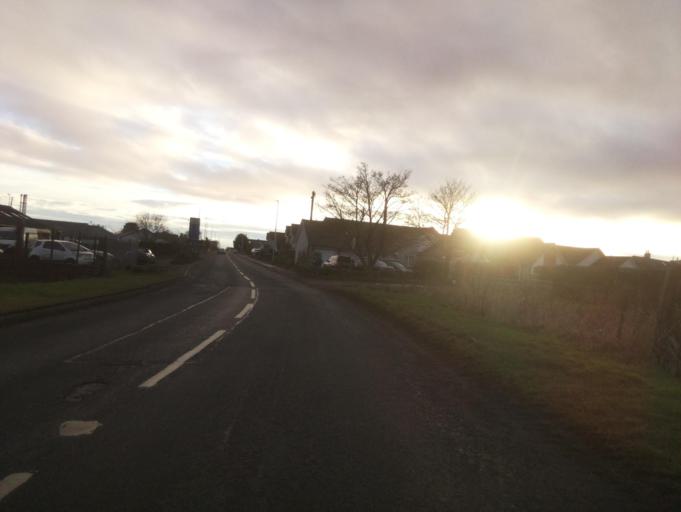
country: GB
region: Scotland
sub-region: Fife
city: Tayport
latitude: 56.5173
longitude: -2.8169
